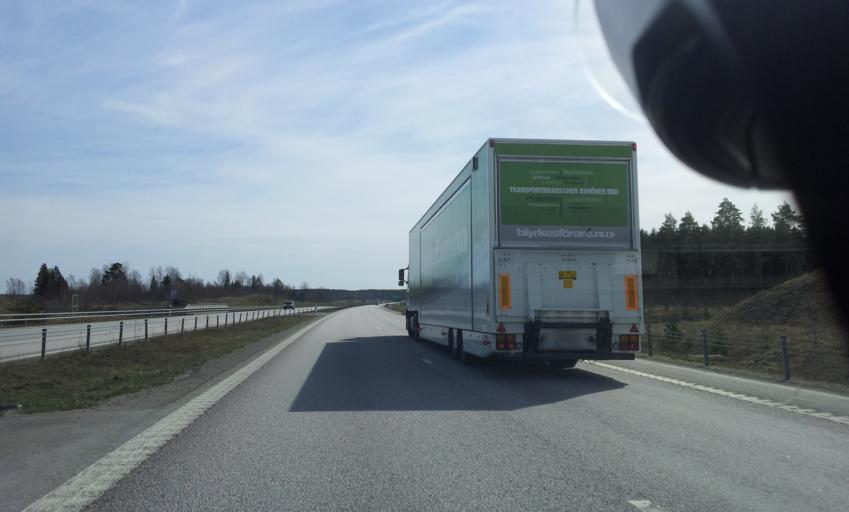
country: SE
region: Uppsala
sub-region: Osthammars Kommun
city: Bjorklinge
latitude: 60.1605
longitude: 17.5351
